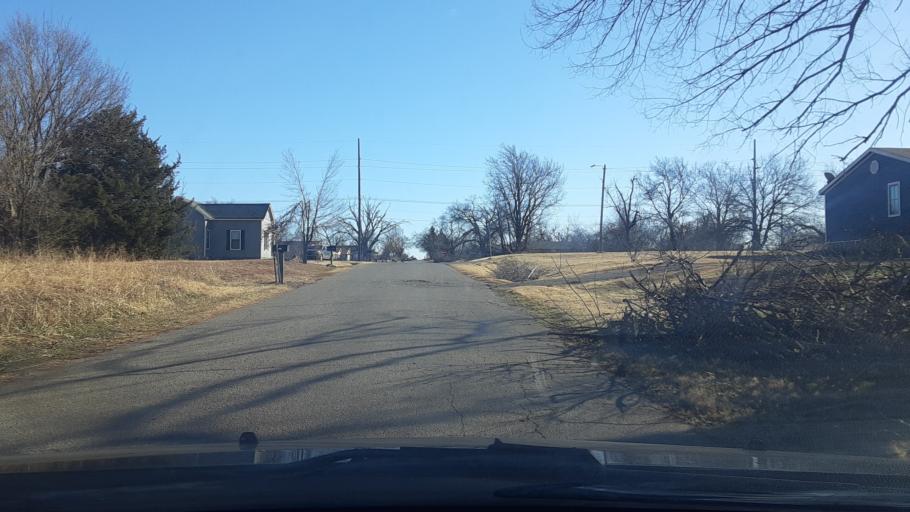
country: US
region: Oklahoma
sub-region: Logan County
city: Guthrie
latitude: 35.8729
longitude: -97.4091
